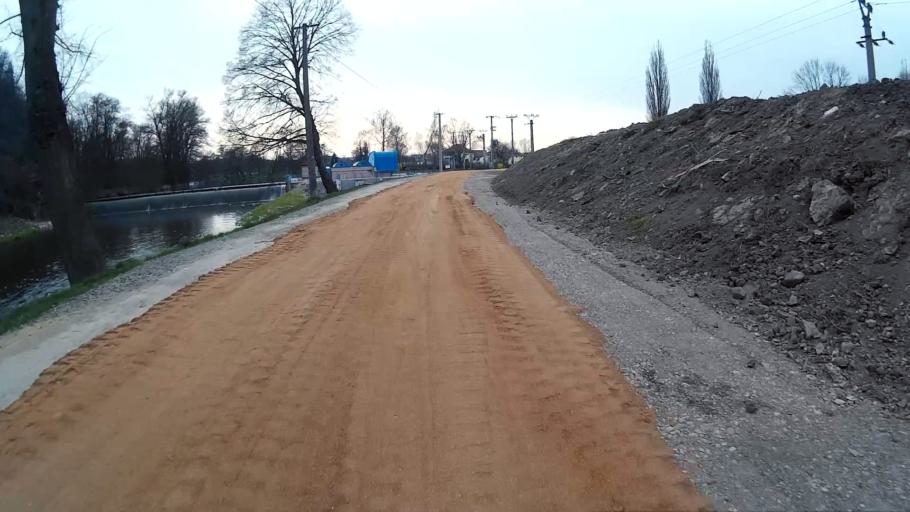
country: CZ
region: South Moravian
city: Ivancice
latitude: 49.0984
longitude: 16.3864
